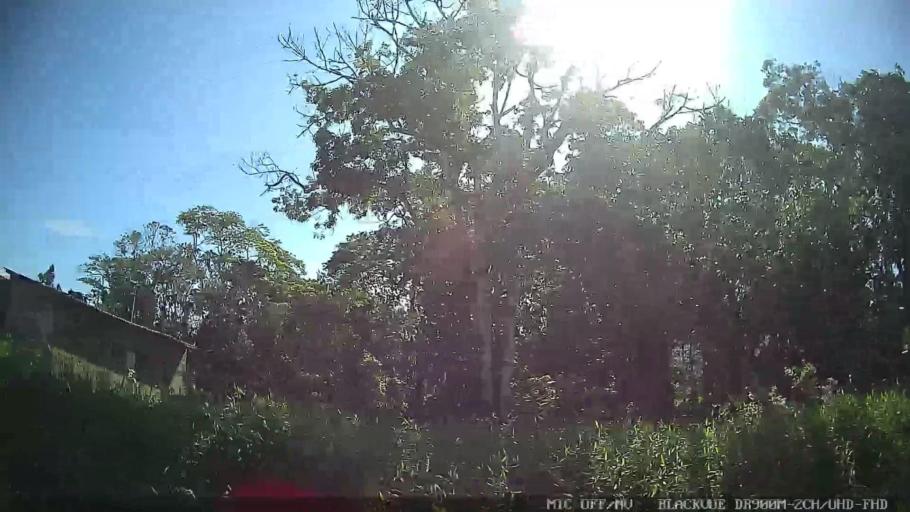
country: BR
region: Sao Paulo
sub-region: Itanhaem
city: Itanhaem
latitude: -24.1469
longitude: -46.7352
